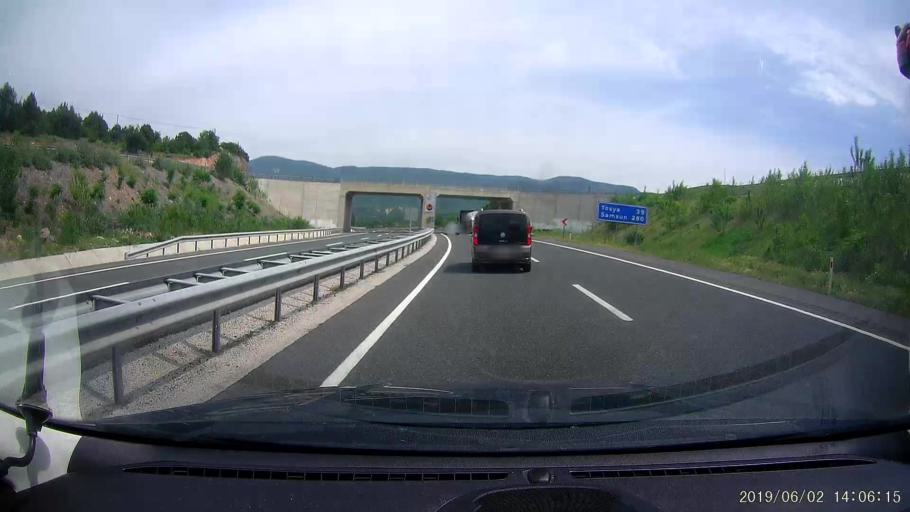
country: TR
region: Cankiri
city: Ilgaz
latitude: 40.8910
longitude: 33.6779
